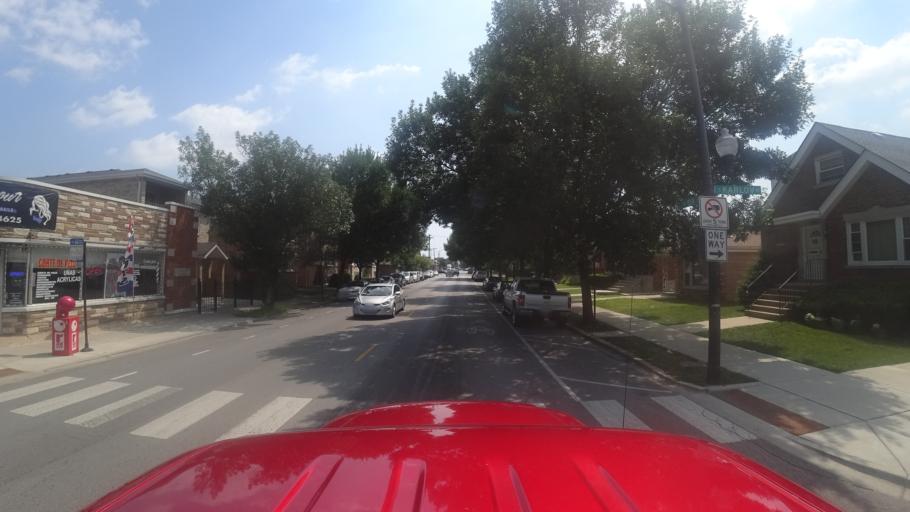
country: US
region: Illinois
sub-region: Cook County
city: Hometown
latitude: 41.7859
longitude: -87.7255
